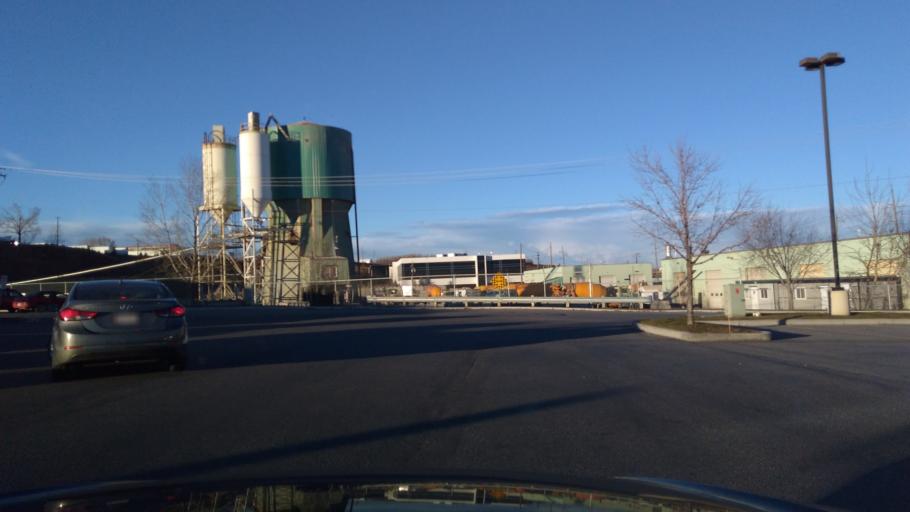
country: CA
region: Alberta
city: Calgary
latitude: 50.9898
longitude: -114.0438
